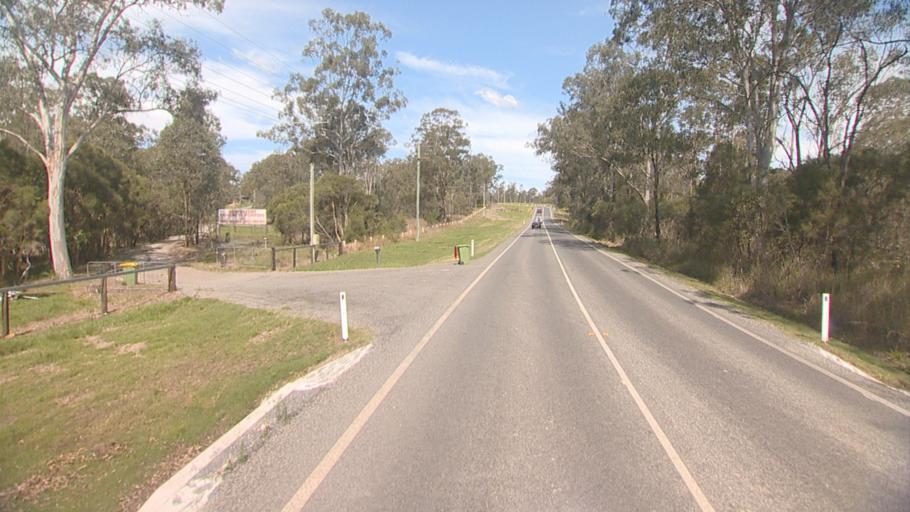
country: AU
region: Queensland
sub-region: Logan
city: Cedar Vale
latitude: -27.8333
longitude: 153.0428
